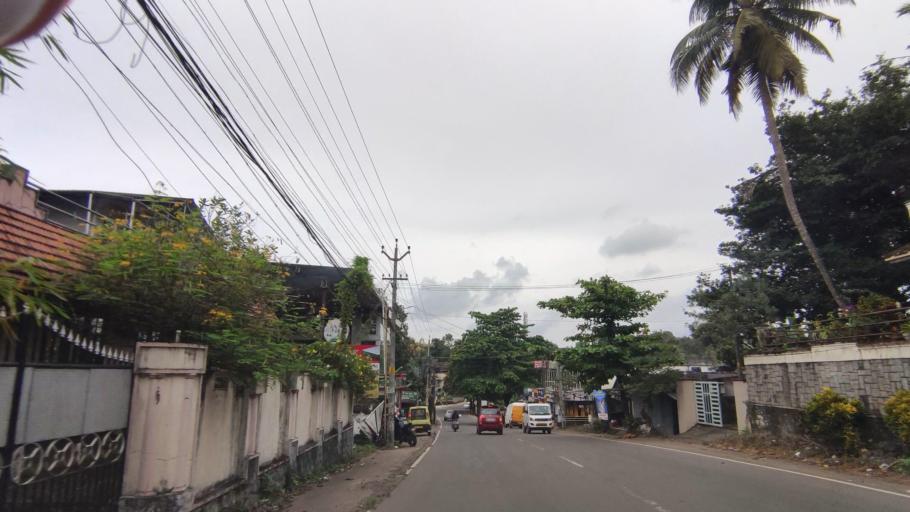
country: IN
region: Kerala
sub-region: Kottayam
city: Kottayam
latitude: 9.6170
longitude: 76.5094
